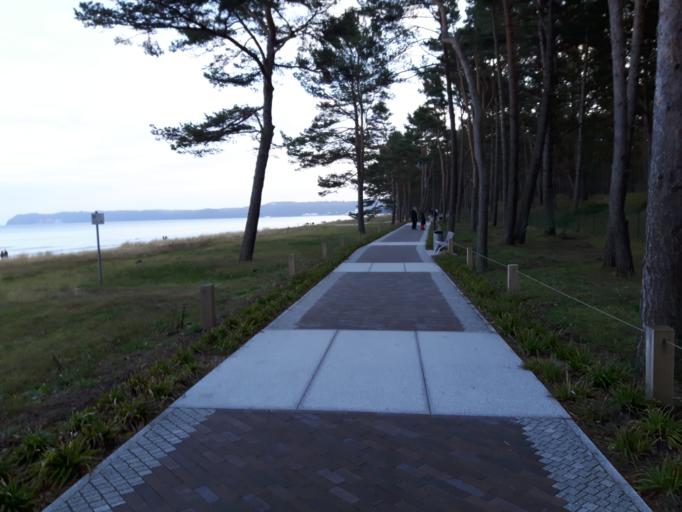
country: DE
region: Mecklenburg-Vorpommern
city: Ostseebad Binz
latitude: 54.4203
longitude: 13.5914
